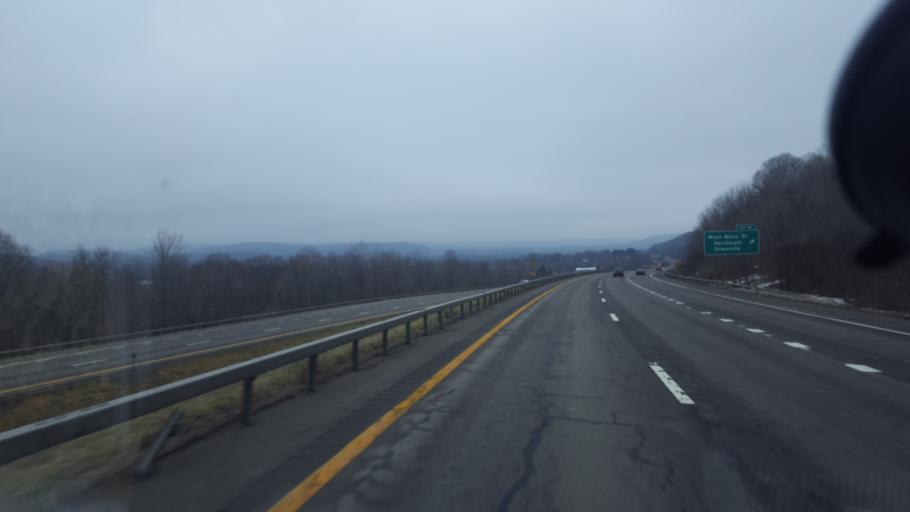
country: US
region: New York
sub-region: Cattaraugus County
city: Randolph
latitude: 42.1617
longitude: -79.0015
